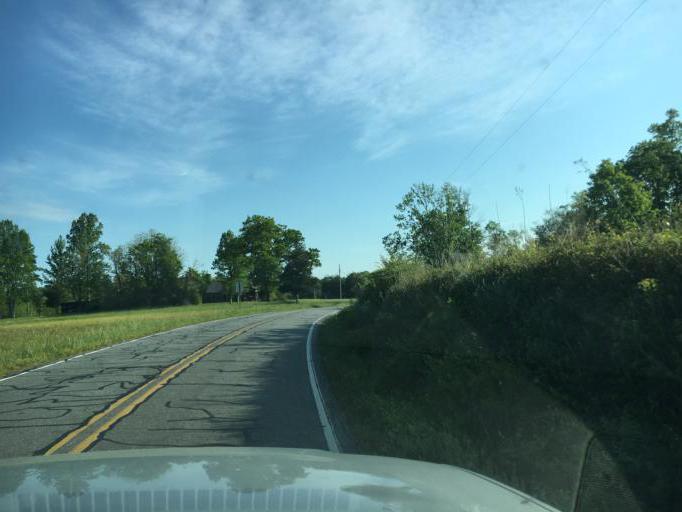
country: US
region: North Carolina
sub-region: Rutherford County
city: Rutherfordton
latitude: 35.3259
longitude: -81.9899
